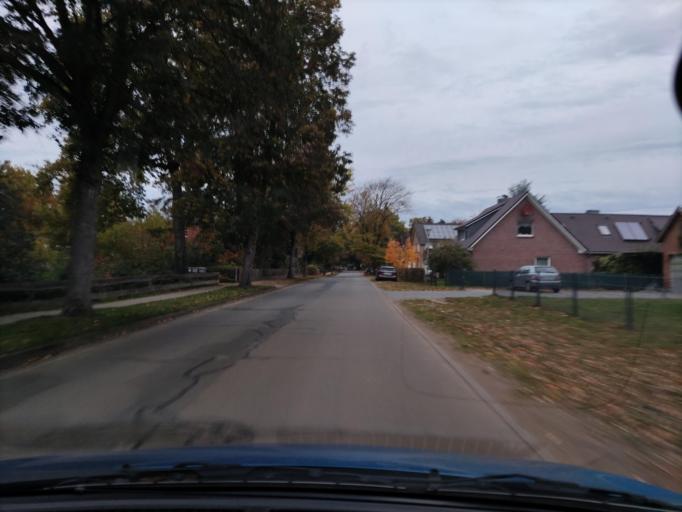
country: DE
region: Lower Saxony
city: Hermannsburg
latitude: 52.8738
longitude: 10.1209
